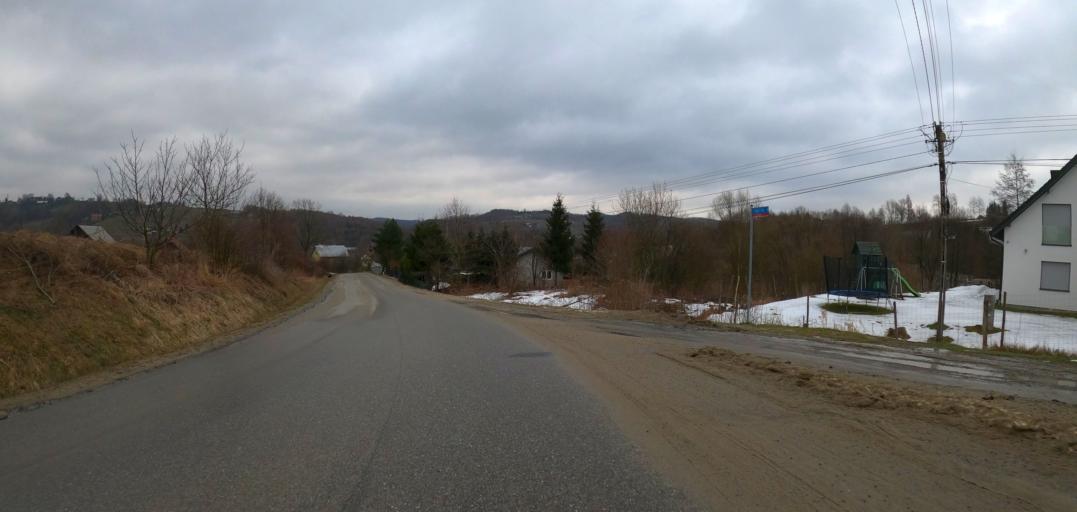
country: PL
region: Subcarpathian Voivodeship
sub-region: Powiat debicki
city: Debica
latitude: 49.9920
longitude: 21.4277
